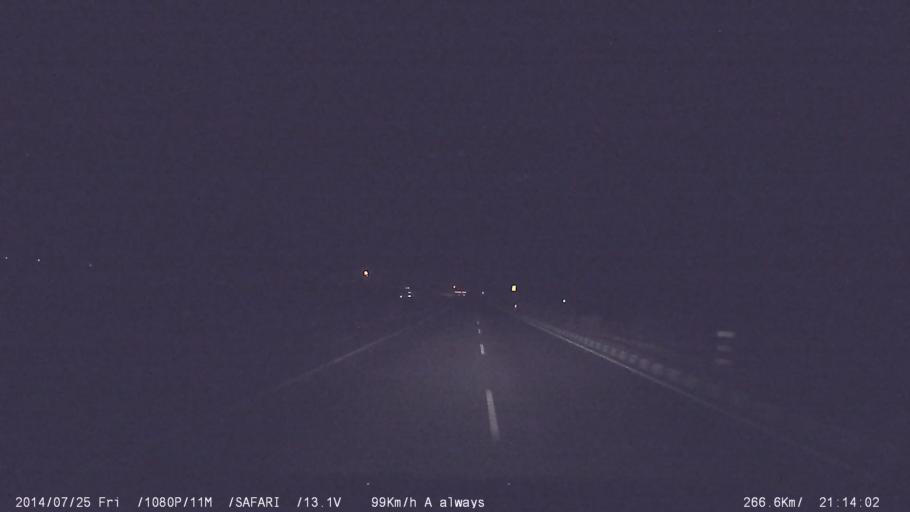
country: IN
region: Tamil Nadu
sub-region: Erode
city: Perundurai
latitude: 11.3424
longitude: 77.6349
